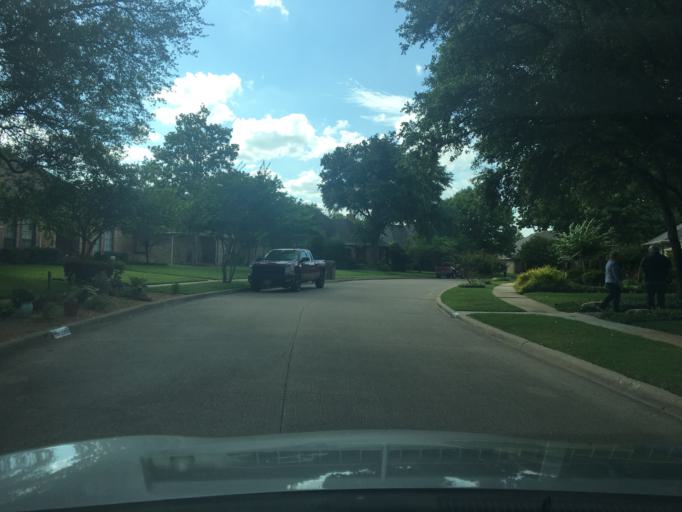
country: US
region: Texas
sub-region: Dallas County
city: Garland
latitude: 32.9355
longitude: -96.6772
